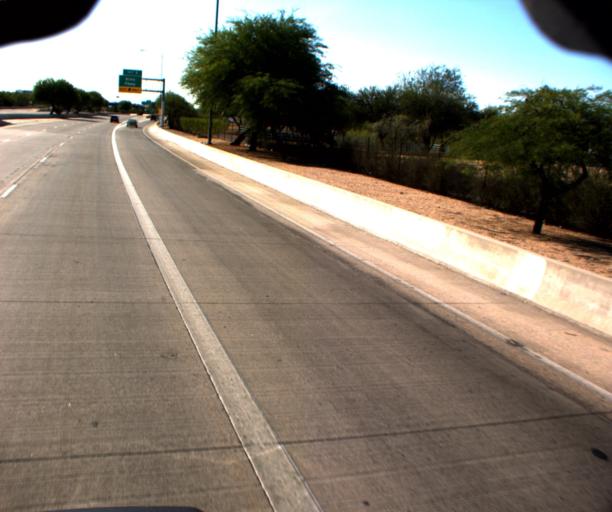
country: US
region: Arizona
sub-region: Pima County
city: Tucson
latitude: 32.2085
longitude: -110.9440
